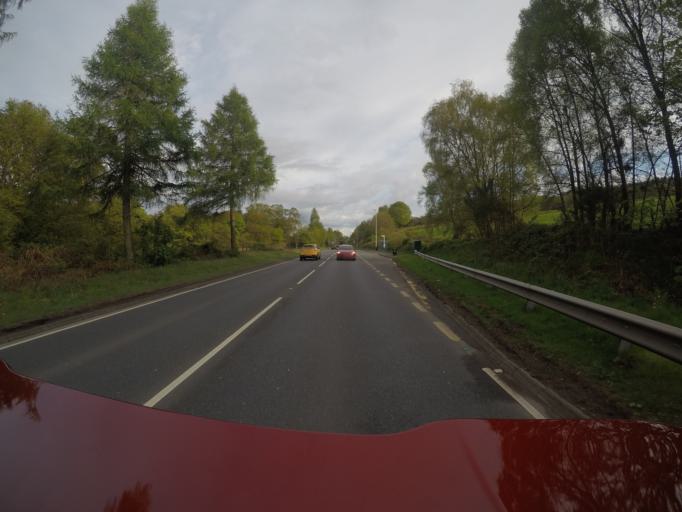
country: GB
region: Scotland
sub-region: West Dunbartonshire
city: Alexandria
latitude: 56.0032
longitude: -4.6008
